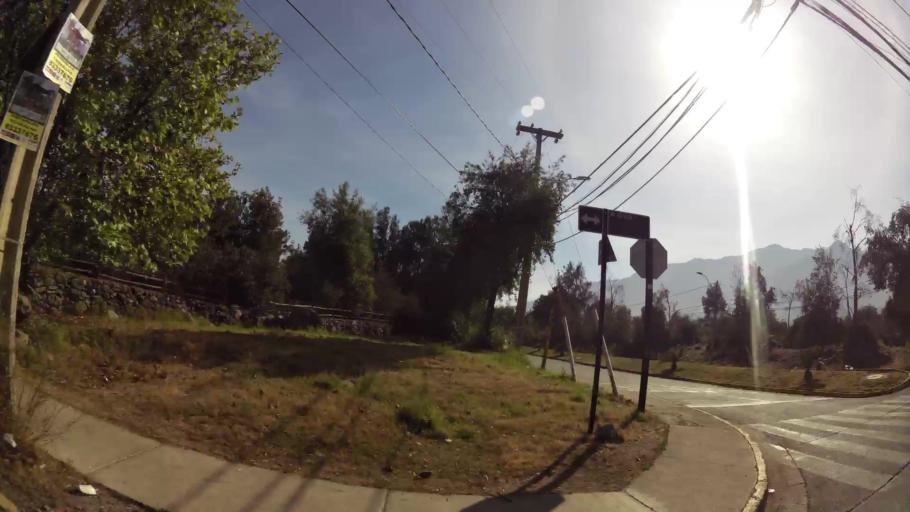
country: CL
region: Santiago Metropolitan
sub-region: Provincia de Santiago
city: Villa Presidente Frei, Nunoa, Santiago, Chile
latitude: -33.5019
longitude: -70.5330
